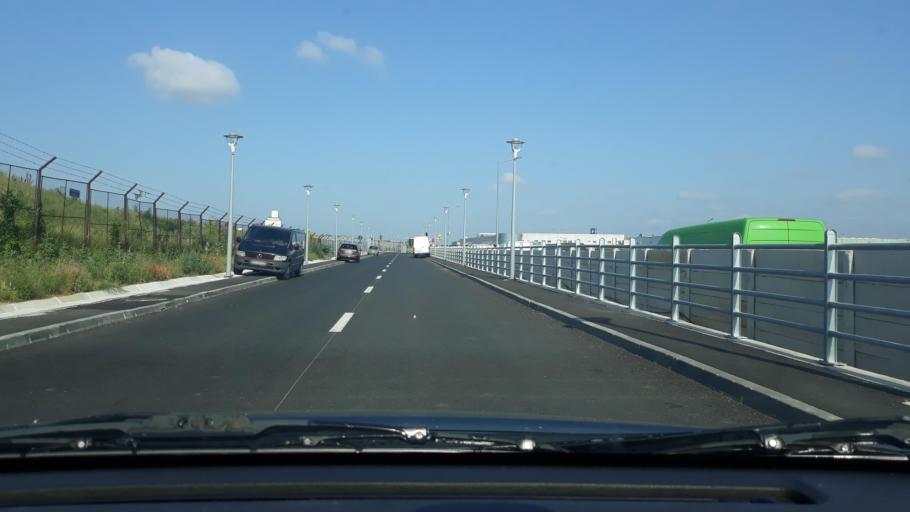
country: RO
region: Bihor
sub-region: Comuna Biharea
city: Oradea
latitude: 47.0389
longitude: 21.9089
